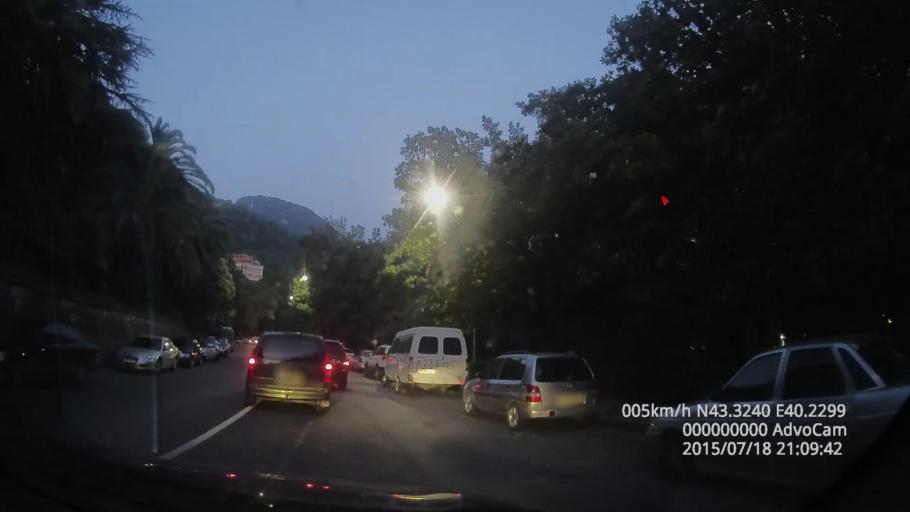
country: GE
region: Abkhazia
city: Gagra
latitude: 43.3240
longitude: 40.2301
